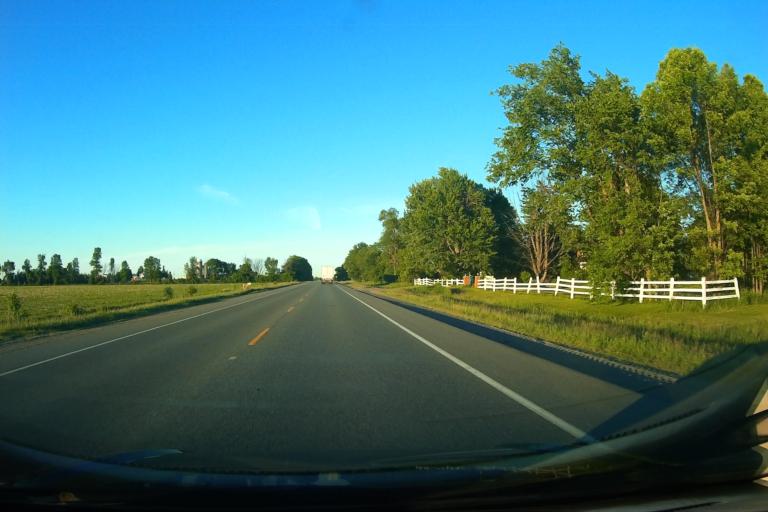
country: CA
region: Ontario
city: Prescott
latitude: 45.0494
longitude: -75.4792
